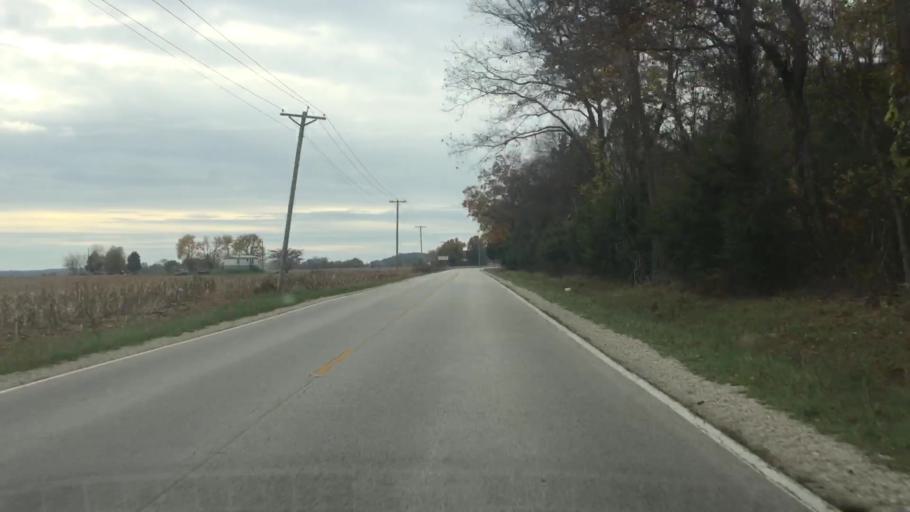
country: US
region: Missouri
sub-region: Gasconade County
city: Hermann
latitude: 38.7226
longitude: -91.4977
